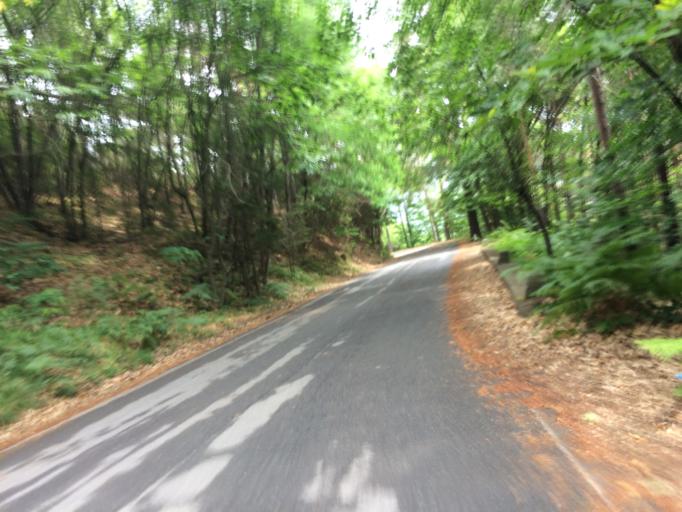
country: IT
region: Liguria
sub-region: Provincia di Imperia
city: Bajardo
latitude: 43.8915
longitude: 7.7333
